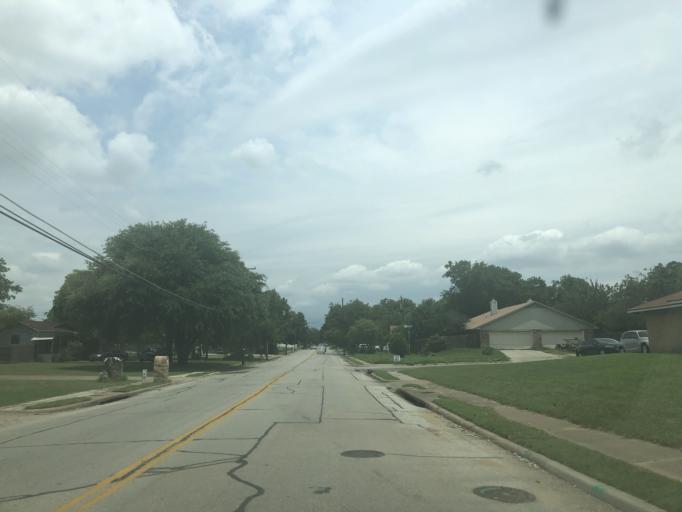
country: US
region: Texas
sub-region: Dallas County
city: Irving
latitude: 32.7962
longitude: -96.9345
